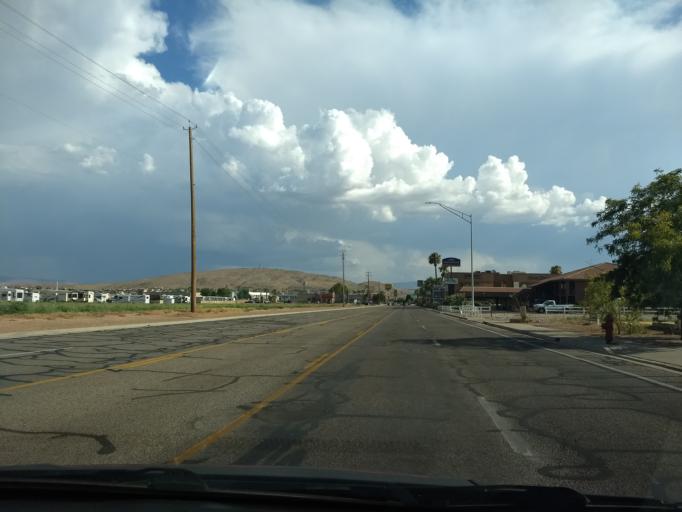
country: US
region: Utah
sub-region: Washington County
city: Saint George
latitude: 37.0914
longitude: -113.5835
